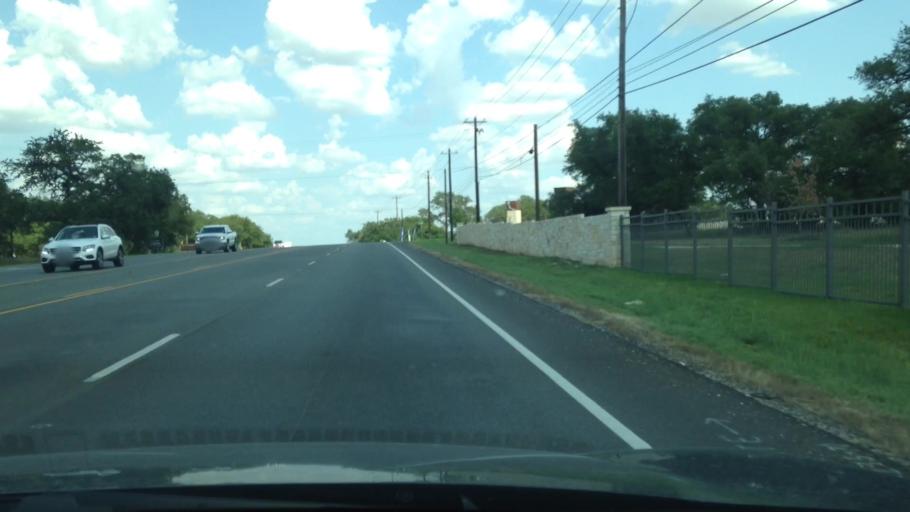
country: US
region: Texas
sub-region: Williamson County
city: Georgetown
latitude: 30.6324
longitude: -97.7636
